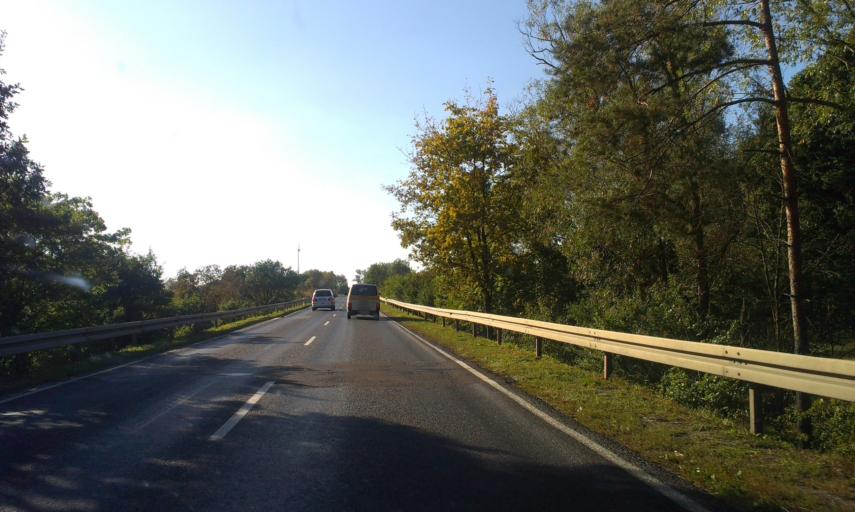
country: PL
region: Kujawsko-Pomorskie
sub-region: Powiat swiecki
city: Swiecie
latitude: 53.4178
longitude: 18.3541
